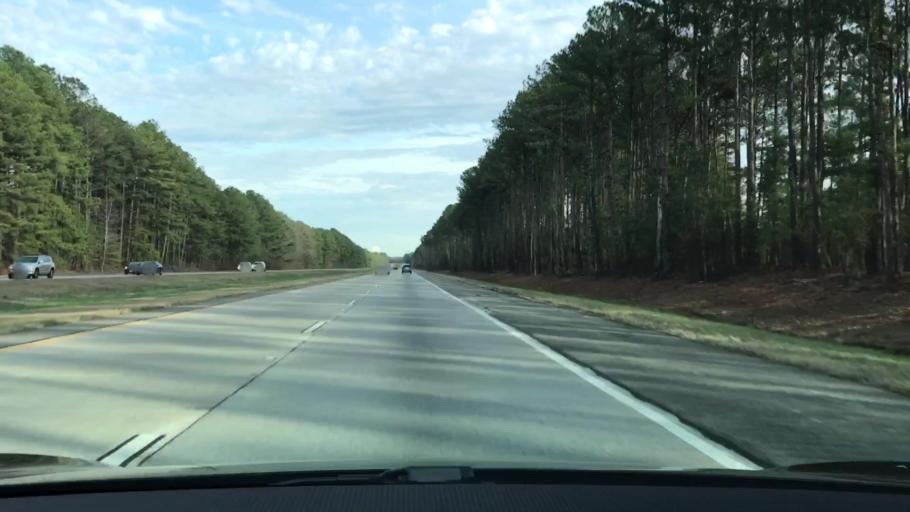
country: US
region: Georgia
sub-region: Taliaferro County
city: Crawfordville
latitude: 33.5312
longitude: -82.9824
